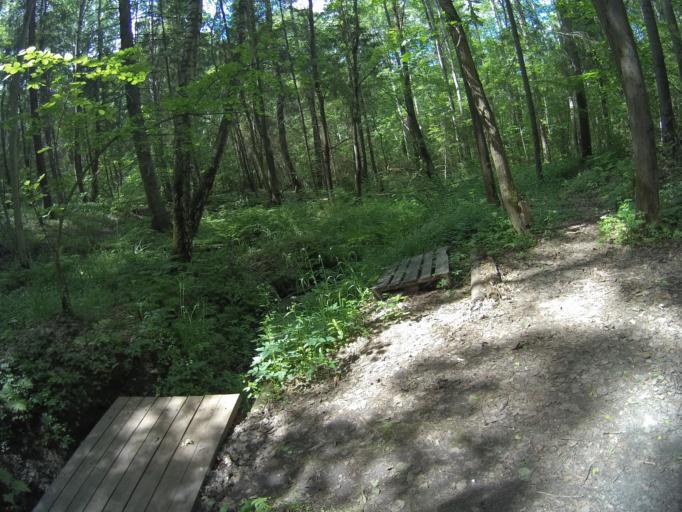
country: RU
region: Vladimir
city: Raduzhnyy
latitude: 56.0224
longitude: 40.2770
